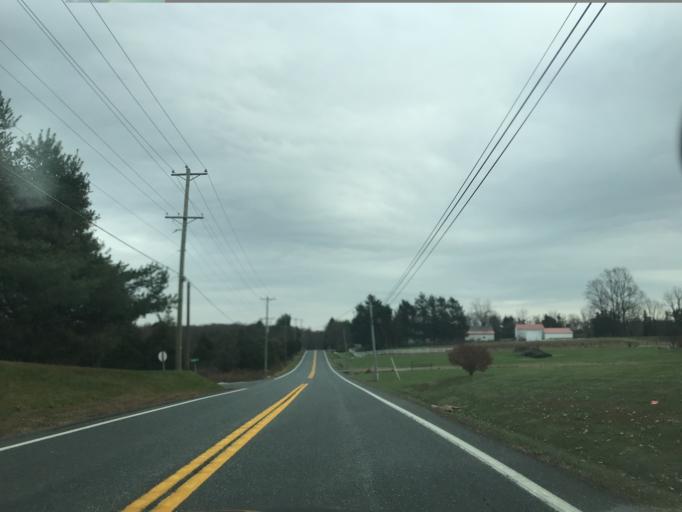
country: US
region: Pennsylvania
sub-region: York County
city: Susquehanna Trails
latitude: 39.6665
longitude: -76.3504
